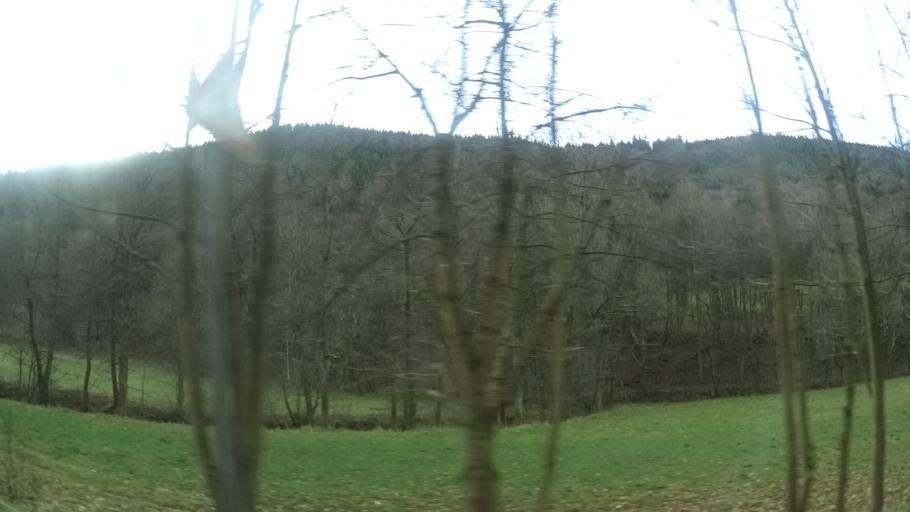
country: DE
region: Thuringia
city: Sitzendorf
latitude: 50.6239
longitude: 11.1888
